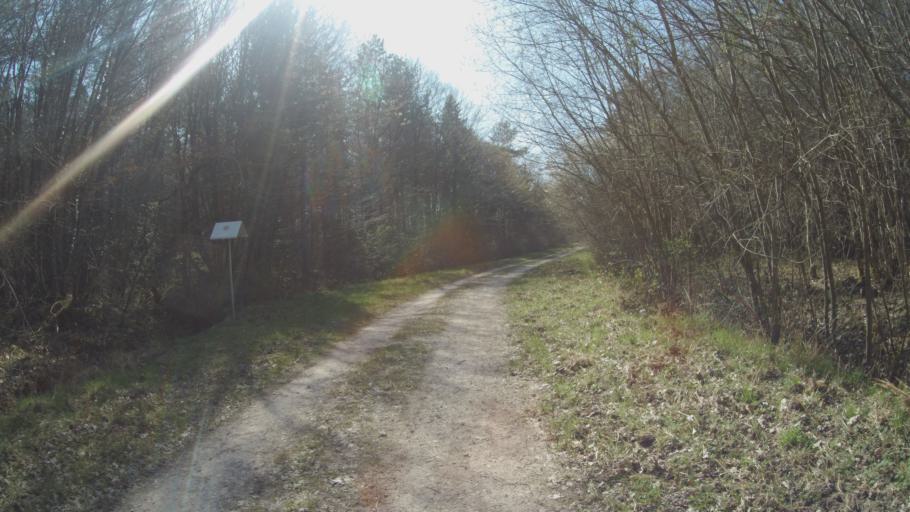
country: FR
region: Centre
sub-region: Departement du Loiret
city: Chanteau
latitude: 47.9513
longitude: 1.9605
